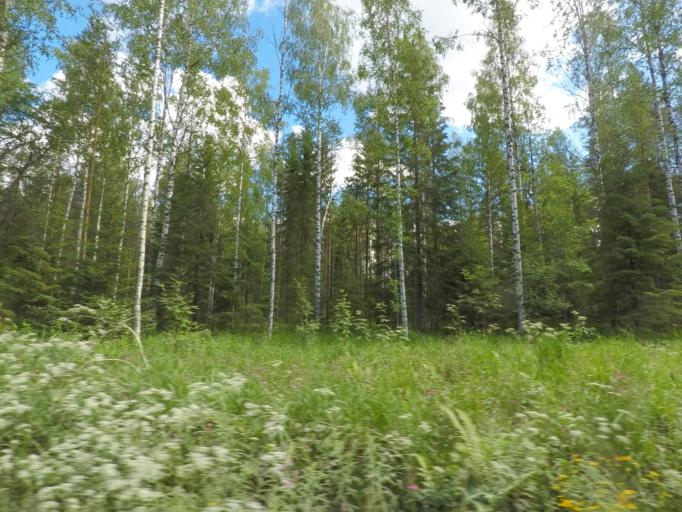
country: FI
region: Central Finland
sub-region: Jyvaeskylae
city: Hankasalmi
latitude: 62.4350
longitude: 26.6478
